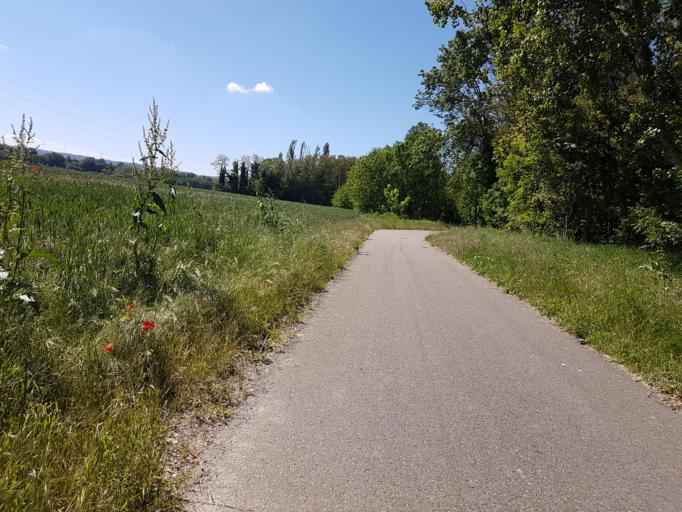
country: FR
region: Rhone-Alpes
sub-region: Departement de la Drome
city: Andancette
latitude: 45.2628
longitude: 4.8120
